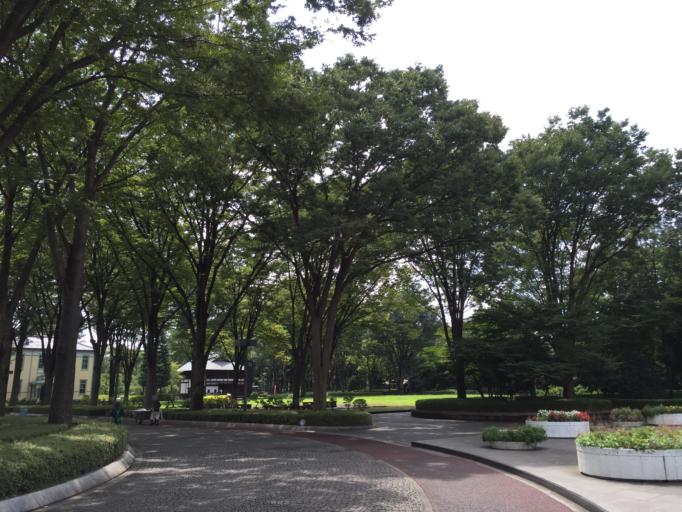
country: JP
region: Tokyo
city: Kokubunji
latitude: 35.6564
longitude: 139.4732
